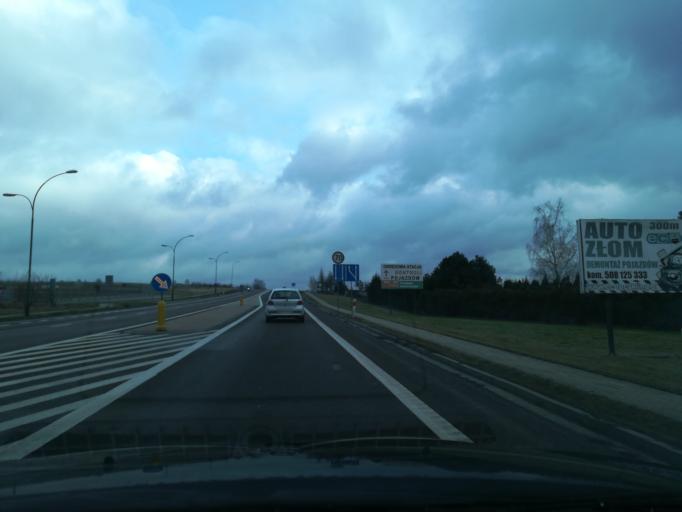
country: PL
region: Subcarpathian Voivodeship
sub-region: Powiat lancucki
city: Kraczkowa
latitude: 50.0463
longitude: 22.1541
